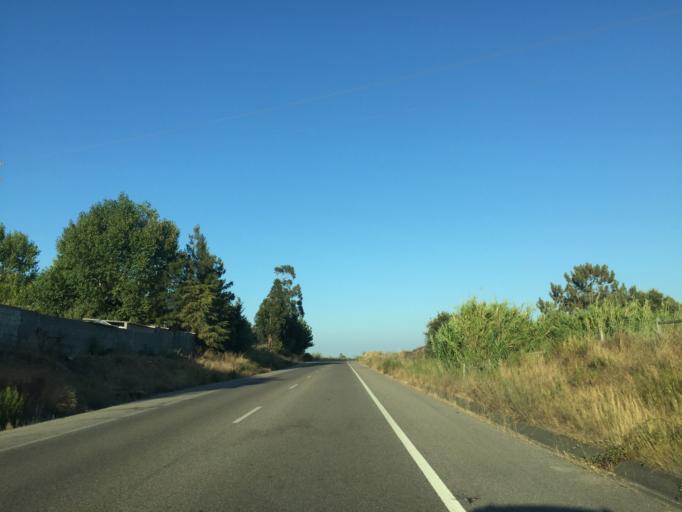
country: PT
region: Lisbon
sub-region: Azambuja
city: Aveiras de Cima
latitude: 39.1537
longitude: -8.8775
